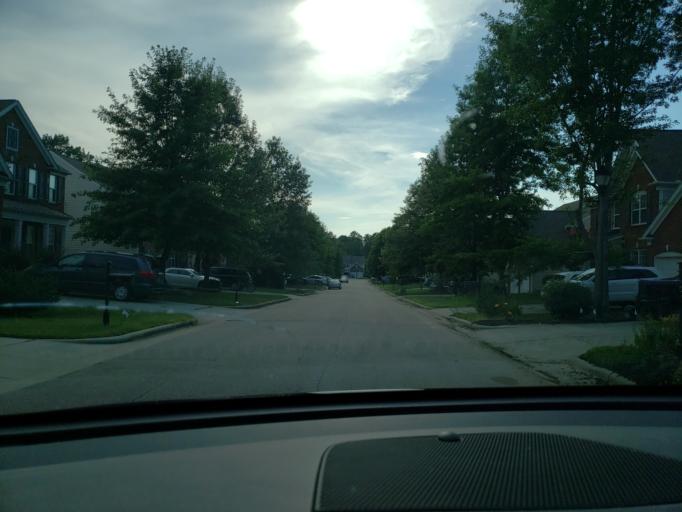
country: US
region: North Carolina
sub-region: Wake County
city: Green Level
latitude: 35.8200
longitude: -78.9095
